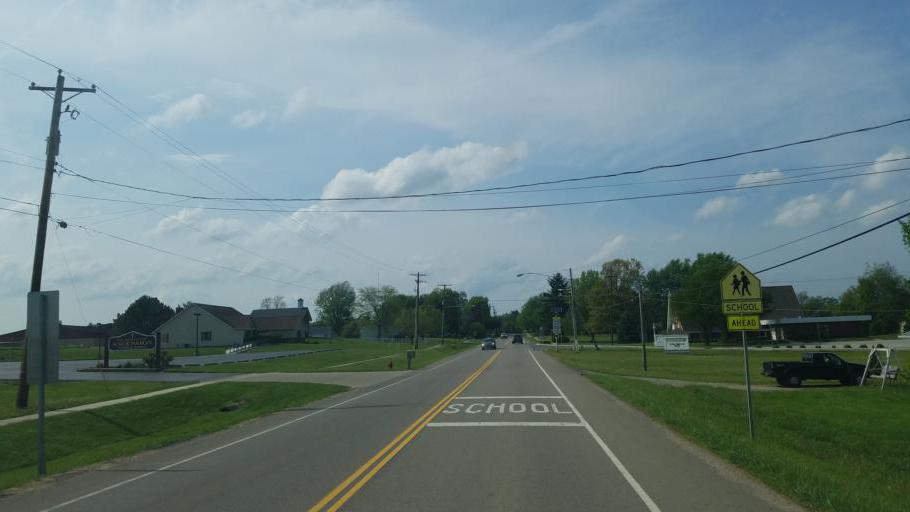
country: US
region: Ohio
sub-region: Licking County
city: Johnstown
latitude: 40.1452
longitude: -82.6767
